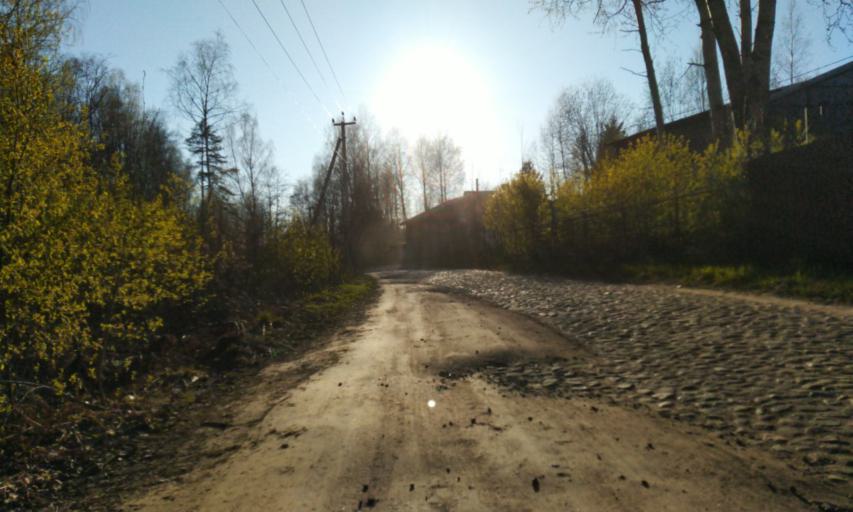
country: RU
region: Leningrad
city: Toksovo
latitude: 60.1399
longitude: 30.5645
